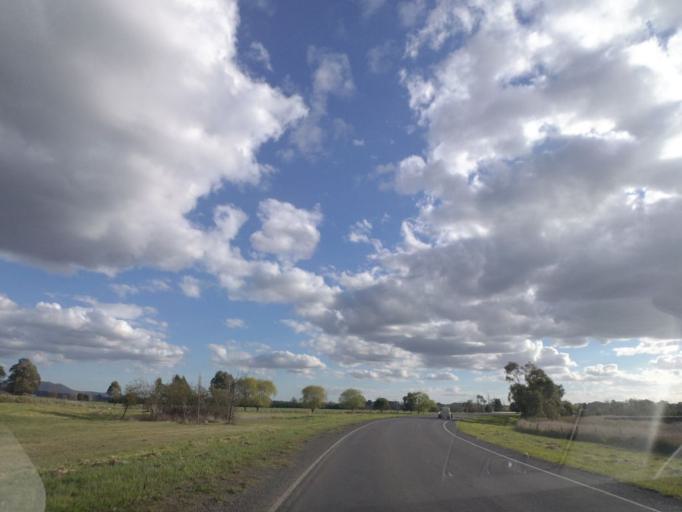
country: AU
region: Victoria
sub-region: Yarra Ranges
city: Yarra Glen
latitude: -37.6992
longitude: 145.3717
